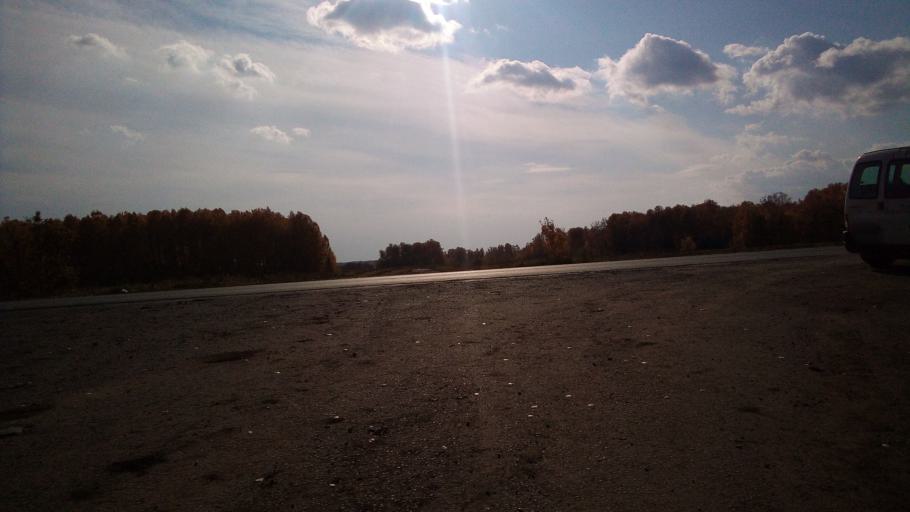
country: RU
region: Chelyabinsk
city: Chebarkul'
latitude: 54.9736
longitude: 60.5131
